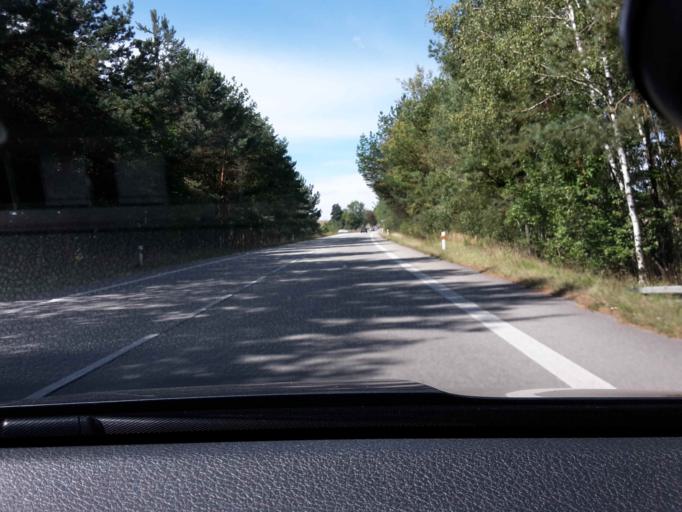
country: CZ
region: Jihocesky
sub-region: Okres Jindrichuv Hradec
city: Jindrichuv Hradec
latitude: 49.1543
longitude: 14.9834
